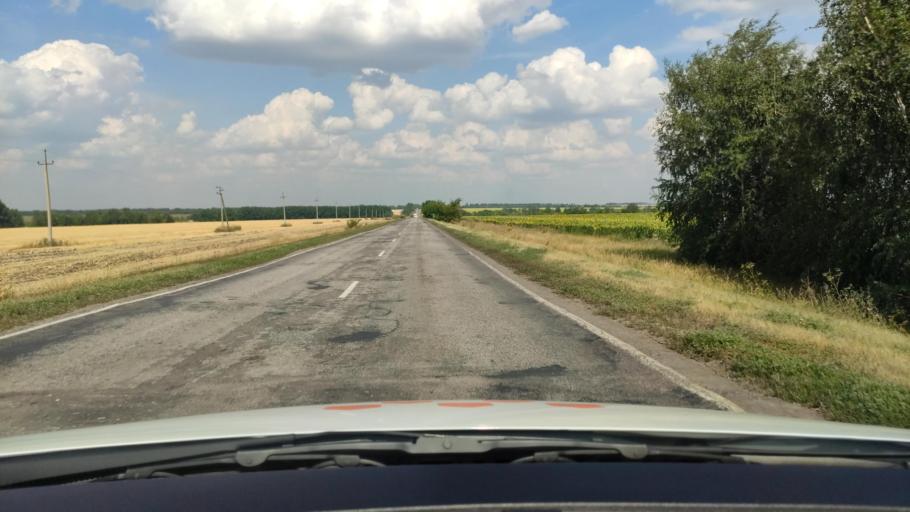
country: RU
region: Voronezj
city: Pereleshinskiy
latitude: 51.7391
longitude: 40.3948
